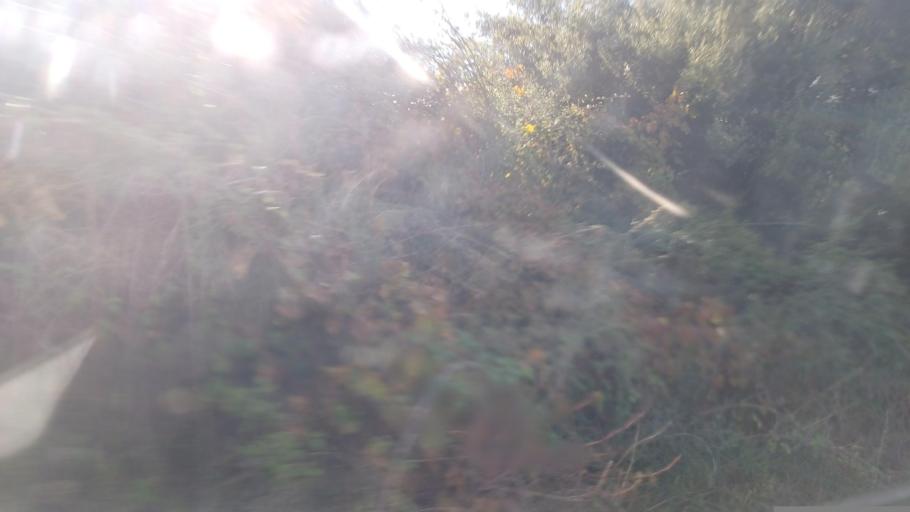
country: CY
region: Pafos
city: Mesogi
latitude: 34.8352
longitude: 32.5493
